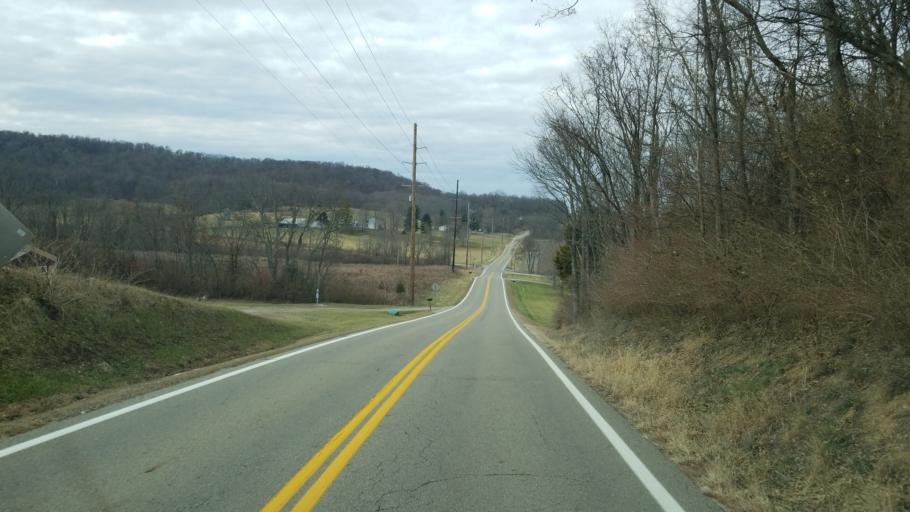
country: US
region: Ohio
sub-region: Ross County
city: Frankfort
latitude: 39.3485
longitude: -83.2122
